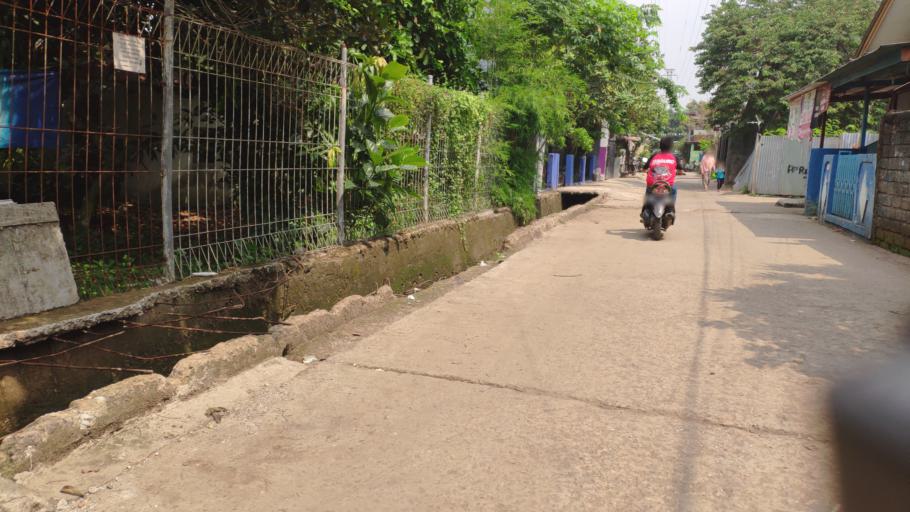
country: ID
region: West Java
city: Depok
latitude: -6.3209
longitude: 106.8275
